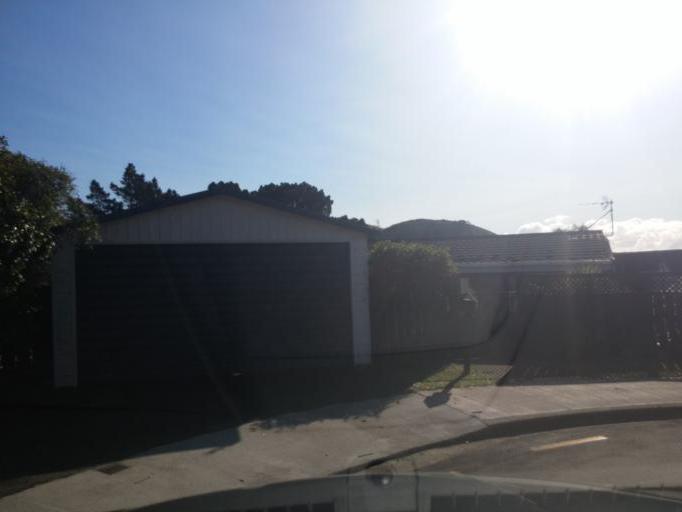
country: NZ
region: Wellington
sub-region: Wellington City
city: Wellington
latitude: -41.2307
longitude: 174.7916
